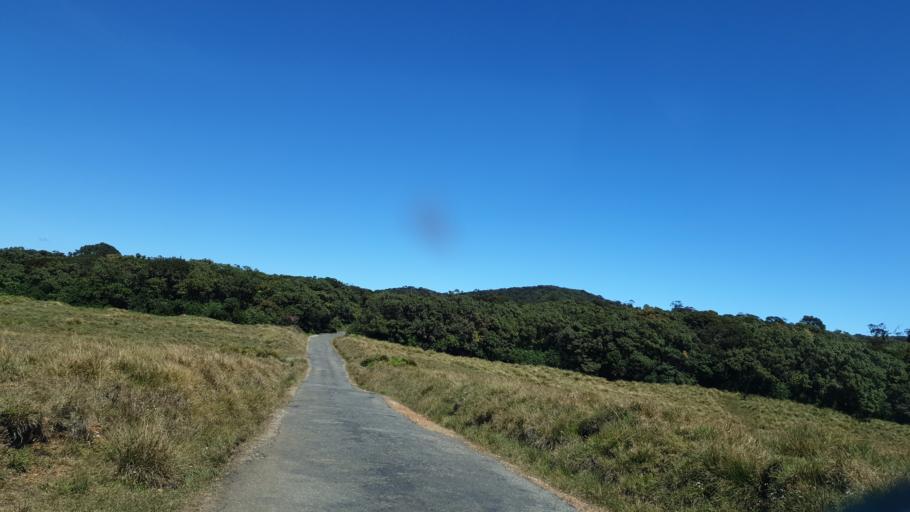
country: LK
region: Central
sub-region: Nuwara Eliya District
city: Nuwara Eliya
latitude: 6.8248
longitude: 80.8054
